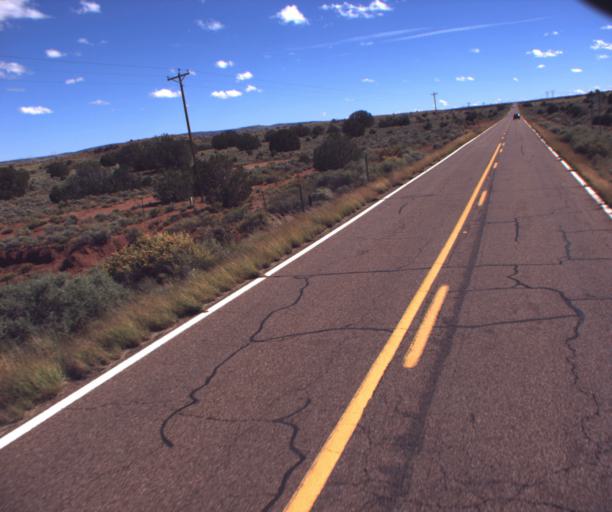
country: US
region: Arizona
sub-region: Apache County
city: Saint Johns
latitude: 34.5791
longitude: -109.6397
